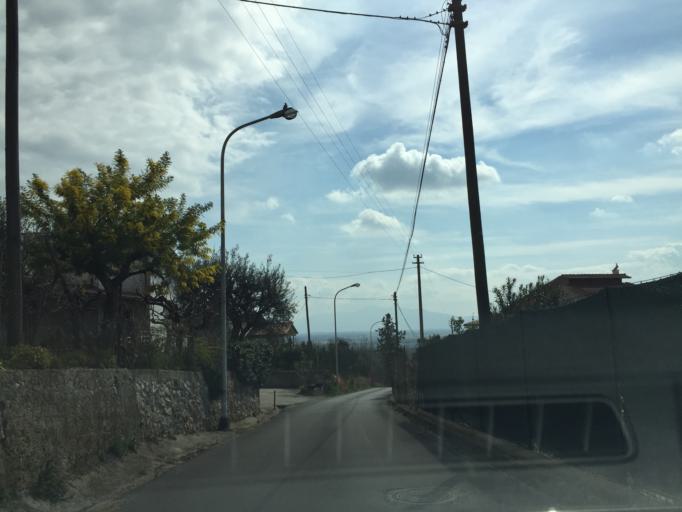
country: IT
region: Latium
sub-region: Provincia di Frosinone
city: Castrocielo
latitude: 41.5257
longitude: 13.7028
